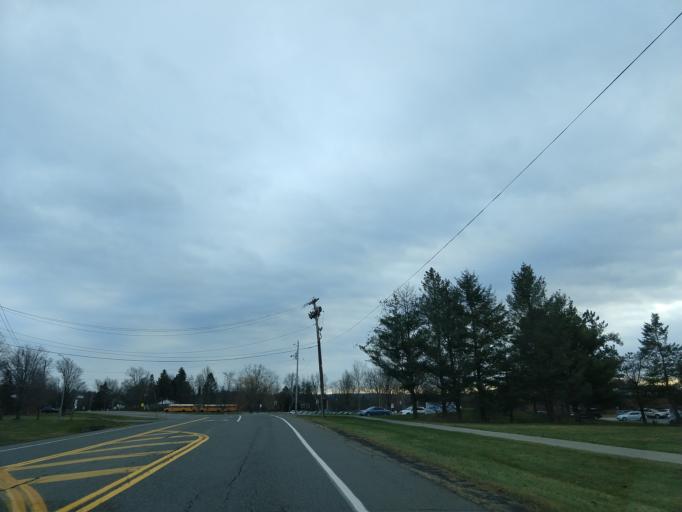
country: US
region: New York
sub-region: Tompkins County
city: Northeast Ithaca
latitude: 42.4769
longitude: -76.4670
